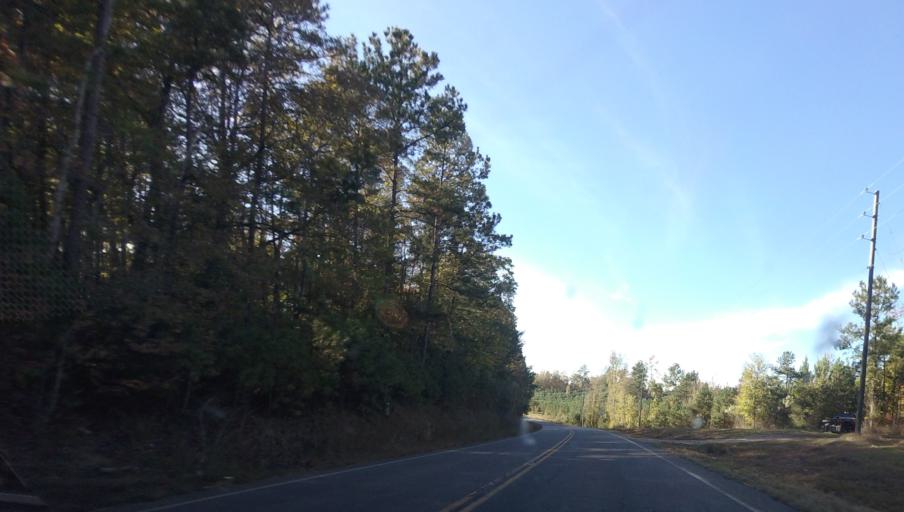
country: US
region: Georgia
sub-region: Talbot County
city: Talbotton
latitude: 32.6803
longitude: -84.6427
